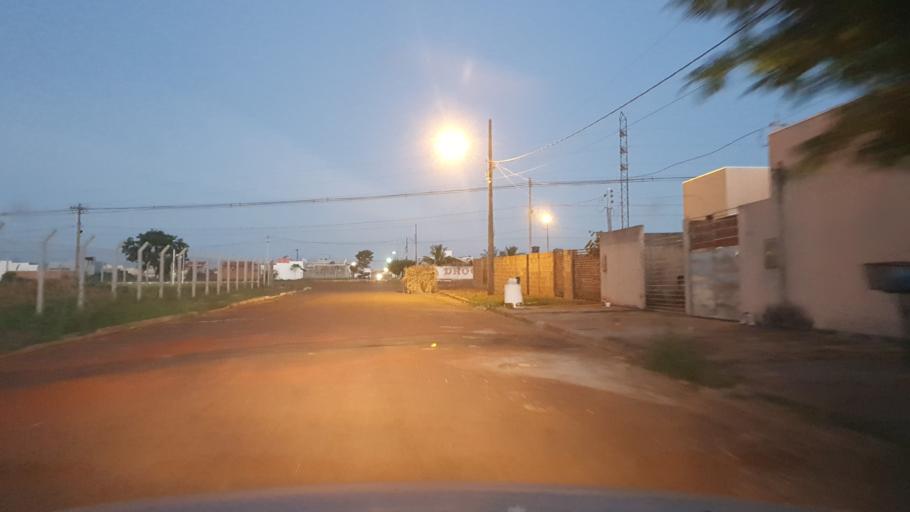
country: BR
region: Mato Grosso
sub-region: Pontes E Lacerda
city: Pontes e Lacerda
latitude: -15.2481
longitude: -59.3233
